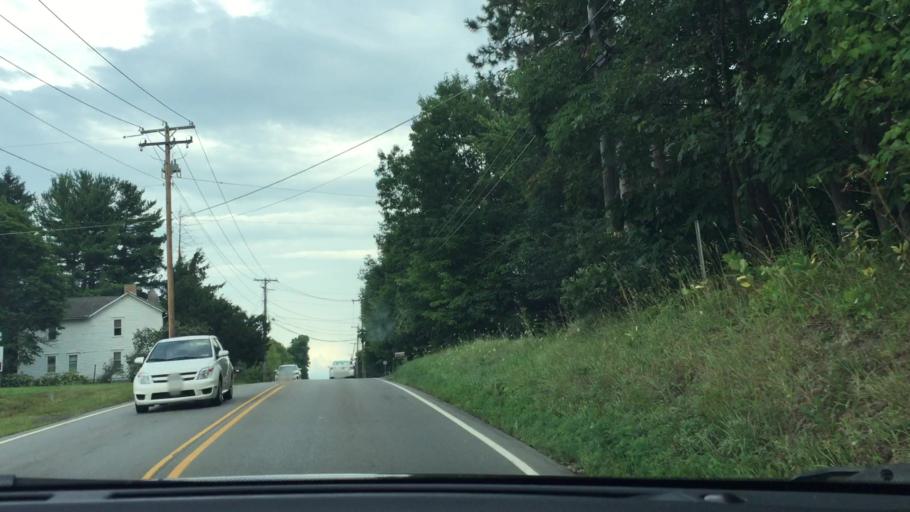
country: US
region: Pennsylvania
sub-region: Butler County
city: Fernway
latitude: 40.6818
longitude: -80.1309
